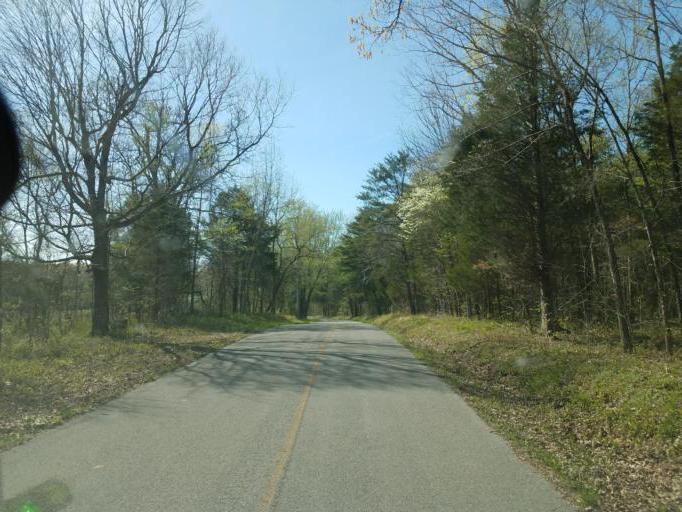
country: US
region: Kentucky
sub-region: Barren County
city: Cave City
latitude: 37.1352
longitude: -85.9729
